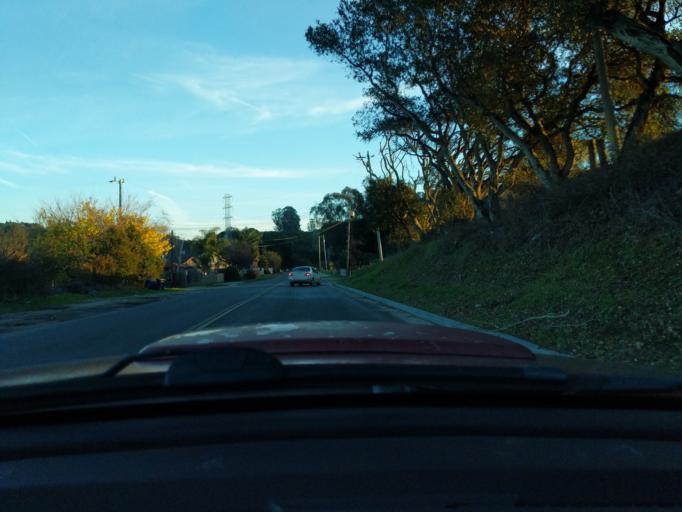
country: US
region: California
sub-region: Monterey County
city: Las Lomas
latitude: 36.8592
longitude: -121.6861
